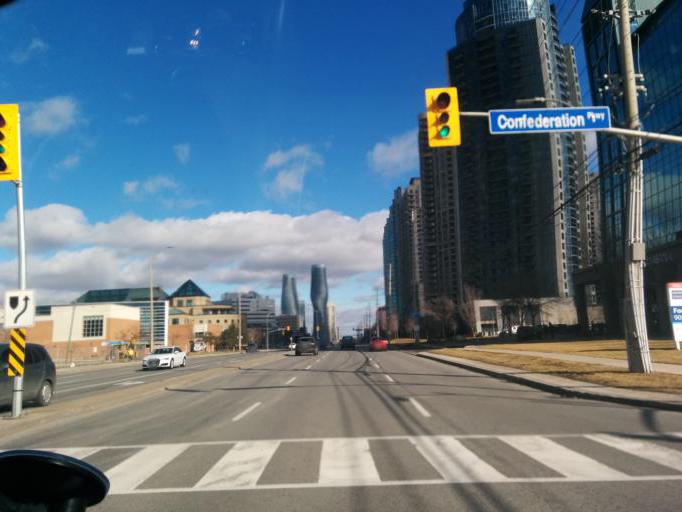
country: CA
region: Ontario
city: Mississauga
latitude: 43.5853
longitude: -79.6448
